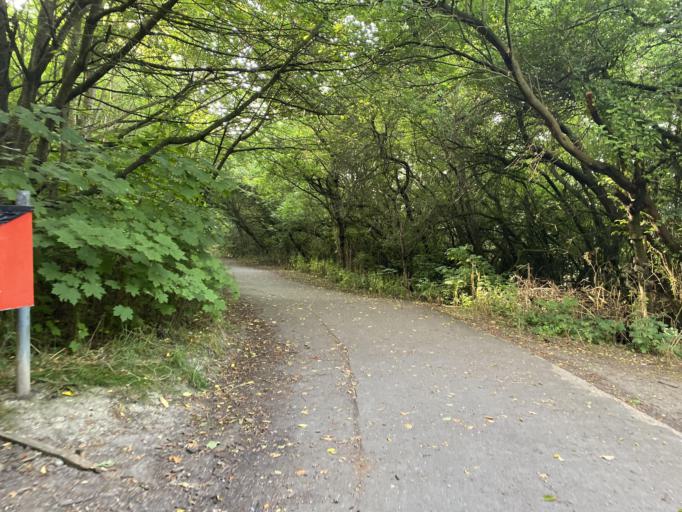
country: GB
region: England
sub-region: Suffolk
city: Haverhill
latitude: 52.0789
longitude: 0.4506
